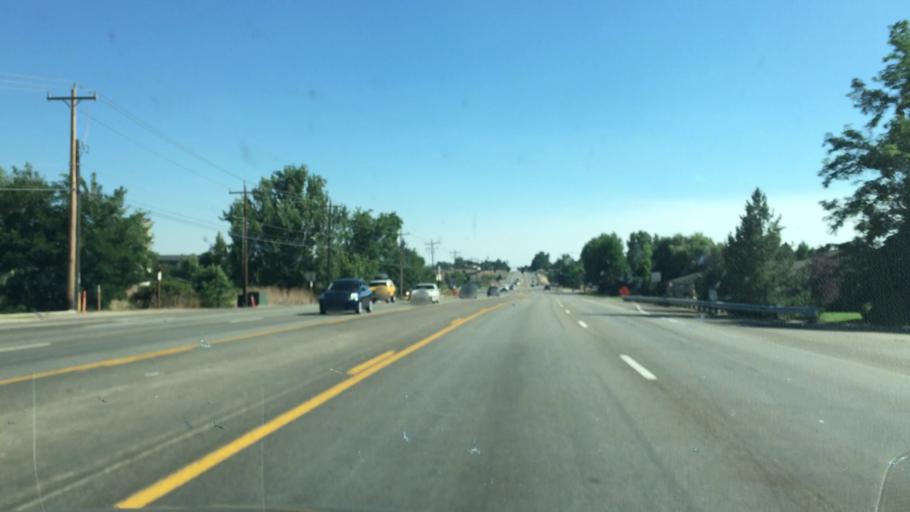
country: US
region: Idaho
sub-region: Ada County
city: Eagle
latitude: 43.6745
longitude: -116.3543
